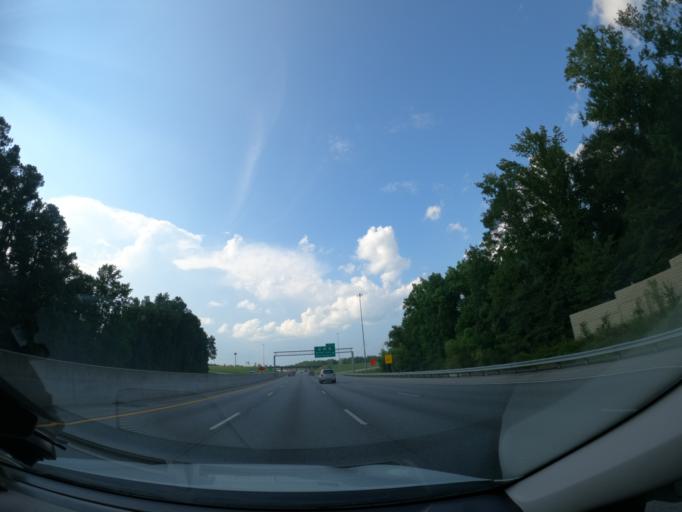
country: US
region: Georgia
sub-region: Columbia County
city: Martinez
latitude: 33.4462
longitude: -82.0729
